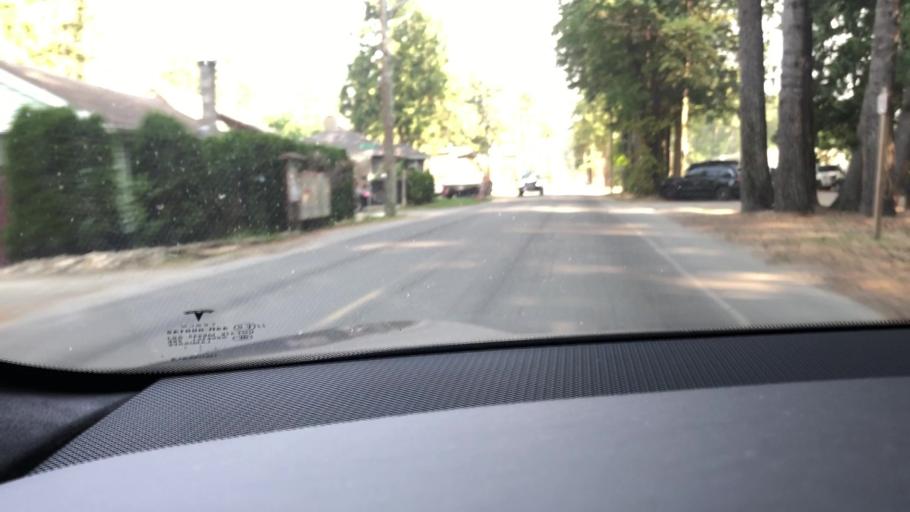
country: CA
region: British Columbia
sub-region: Fraser Valley Regional District
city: Chilliwack
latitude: 49.0711
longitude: -121.9762
